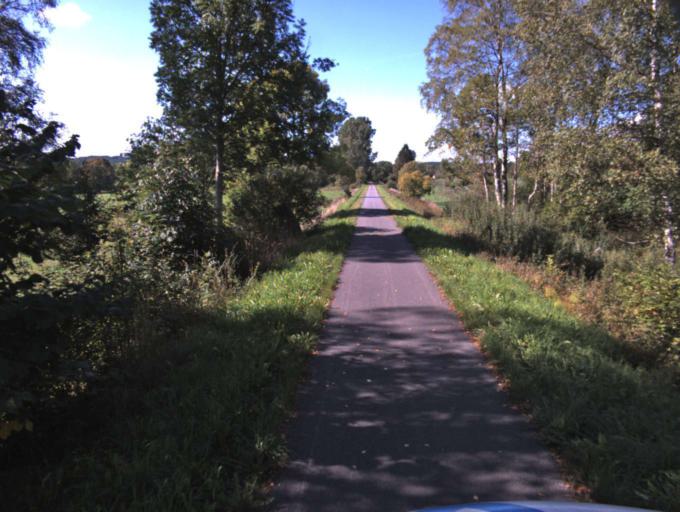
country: SE
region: Vaestra Goetaland
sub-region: Ulricehamns Kommun
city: Ulricehamn
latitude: 57.8005
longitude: 13.3778
